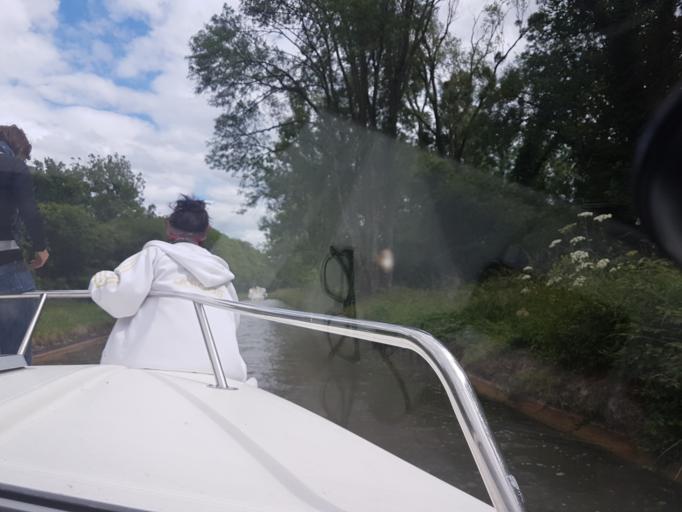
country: FR
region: Bourgogne
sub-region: Departement de l'Yonne
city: Vermenton
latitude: 47.5896
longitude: 3.6373
